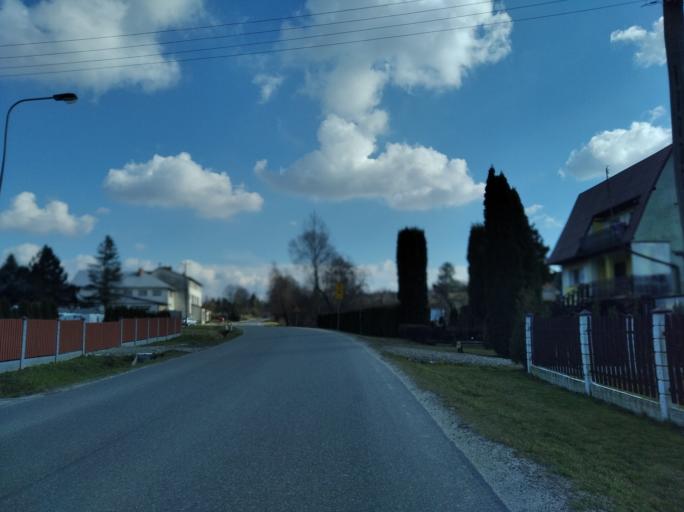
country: PL
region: Subcarpathian Voivodeship
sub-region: Powiat jasielski
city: Kolaczyce
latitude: 49.8538
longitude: 21.4983
